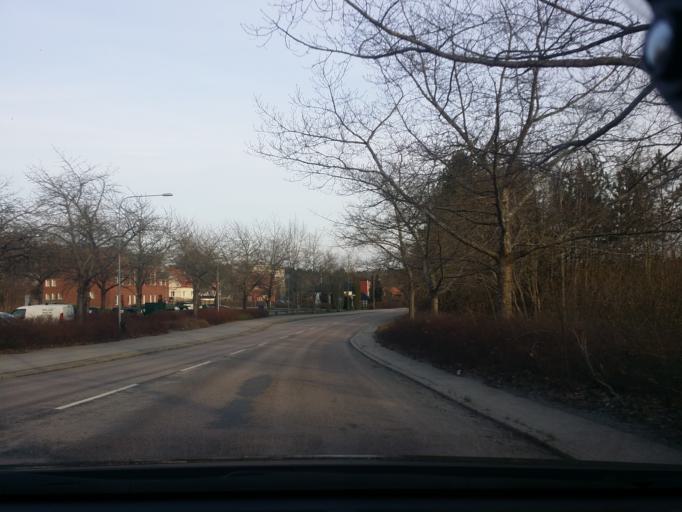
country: SE
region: Uppsala
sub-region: Enkopings Kommun
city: Enkoping
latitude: 59.6402
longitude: 17.1002
